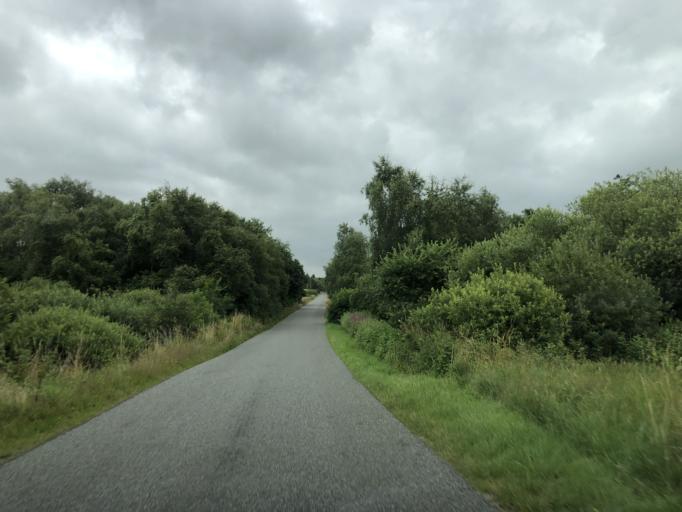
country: DK
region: Central Jutland
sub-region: Herning Kommune
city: Snejbjerg
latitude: 56.1922
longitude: 8.8456
